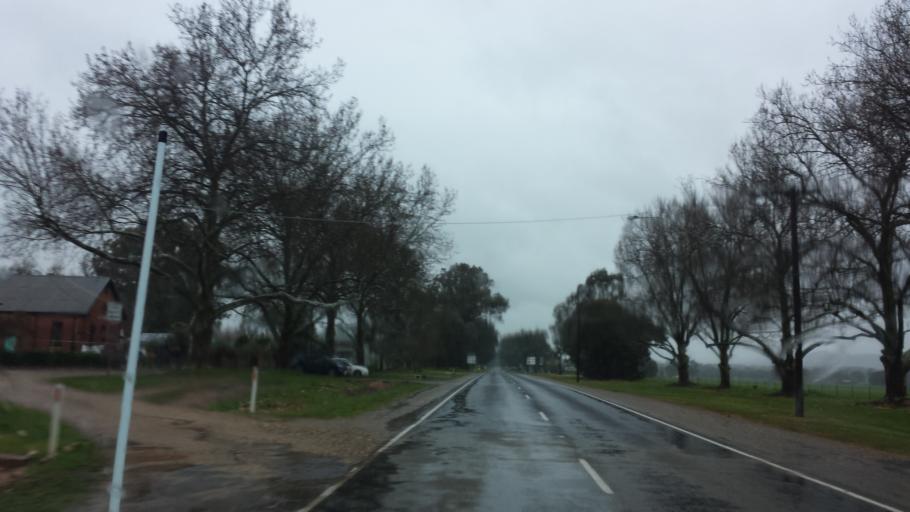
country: AU
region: Victoria
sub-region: Wangaratta
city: Wangaratta
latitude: -36.4353
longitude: 146.5440
